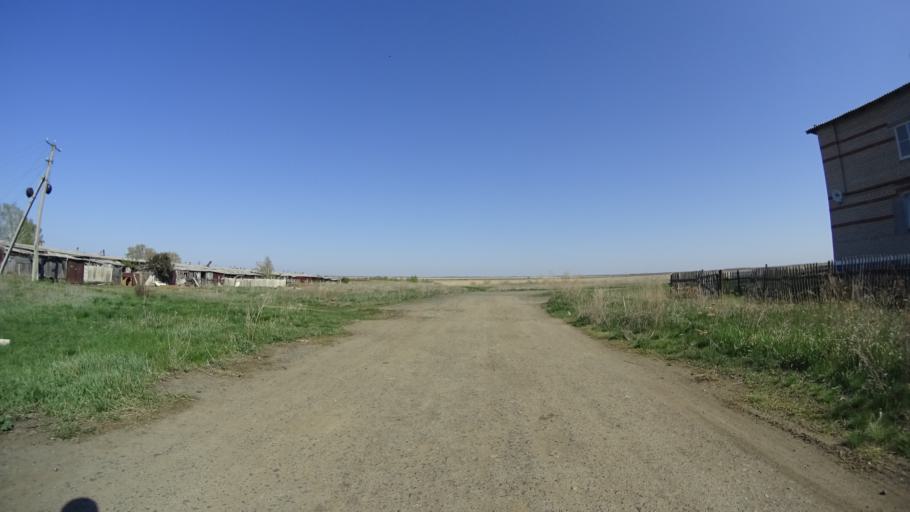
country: RU
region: Chelyabinsk
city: Troitsk
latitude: 54.1902
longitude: 61.5022
